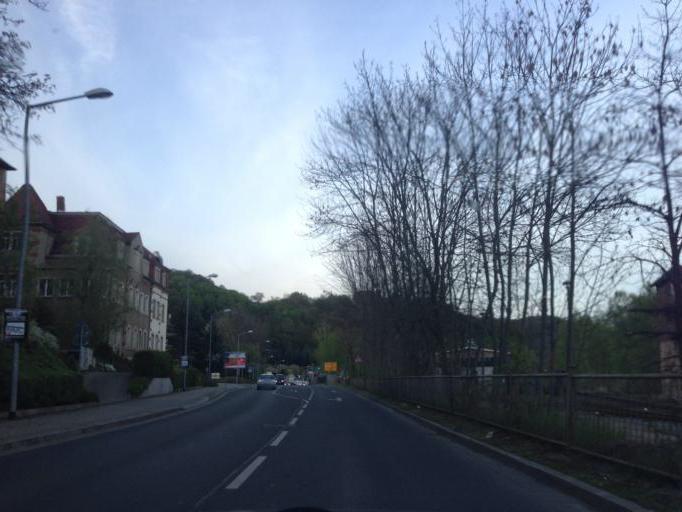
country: DE
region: Saxony
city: Freital
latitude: 51.0134
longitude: 13.6608
